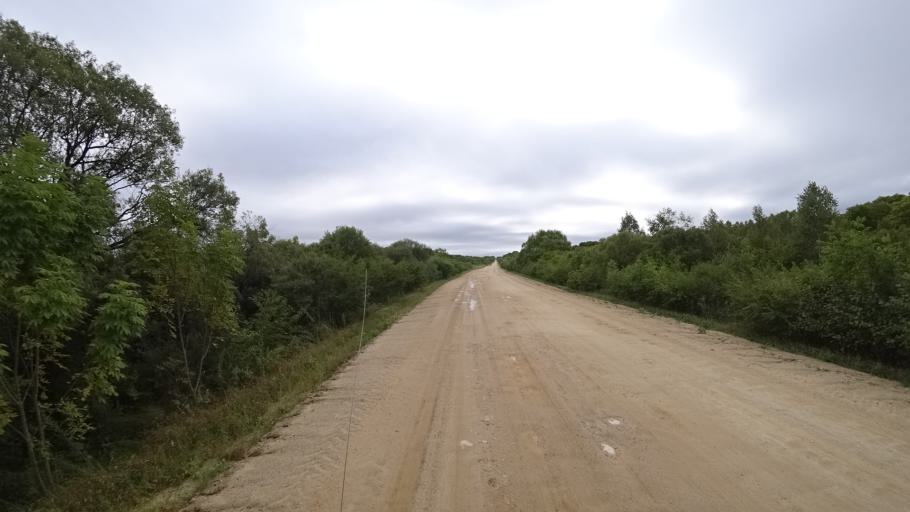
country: RU
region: Primorskiy
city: Rettikhovka
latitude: 44.1224
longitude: 132.6362
